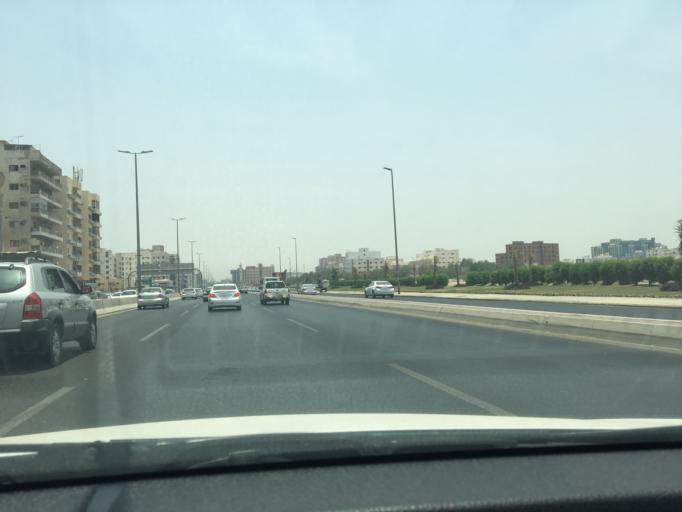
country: SA
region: Makkah
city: Jeddah
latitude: 21.5189
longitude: 39.1927
